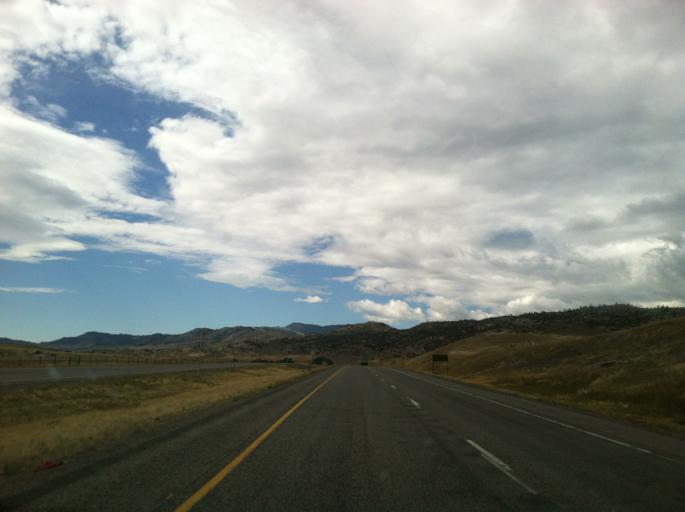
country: US
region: Montana
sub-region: Park County
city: Livingston
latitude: 45.6570
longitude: -110.6289
